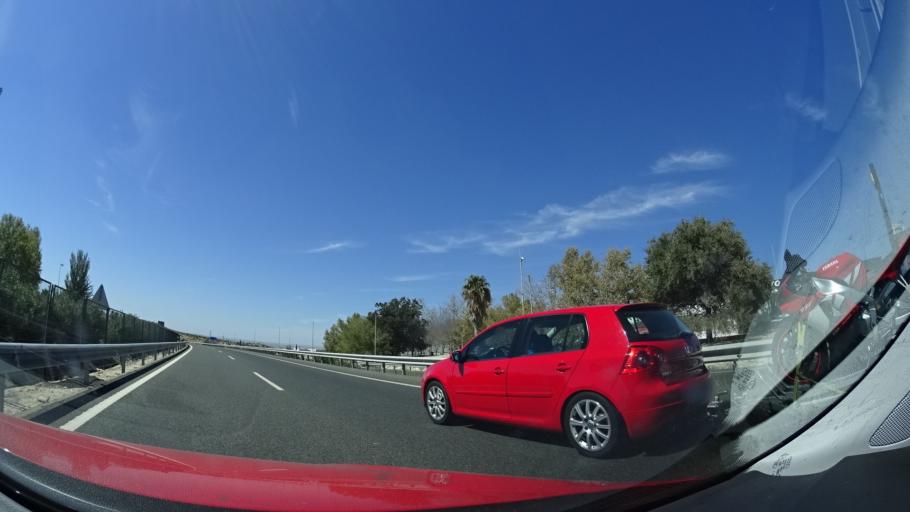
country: ES
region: Andalusia
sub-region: Provincia de Sevilla
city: Estepa
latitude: 37.3024
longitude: -4.8764
